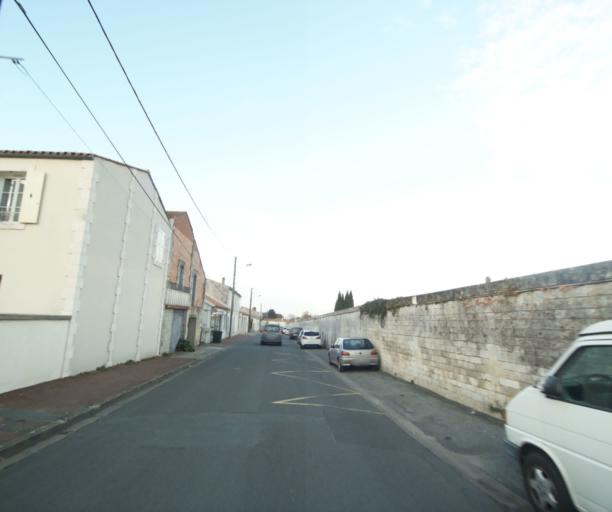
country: FR
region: Poitou-Charentes
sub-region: Departement de la Charente-Maritime
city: Saintes
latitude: 45.7518
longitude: -0.6387
